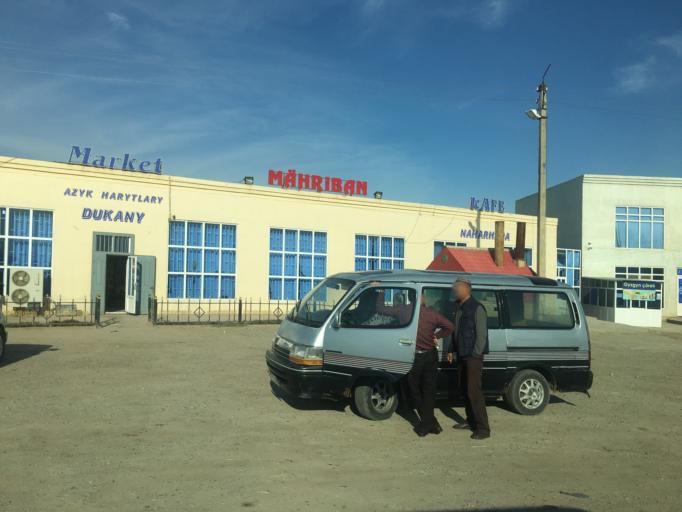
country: TM
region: Mary
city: Mary
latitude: 37.6053
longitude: 61.7427
